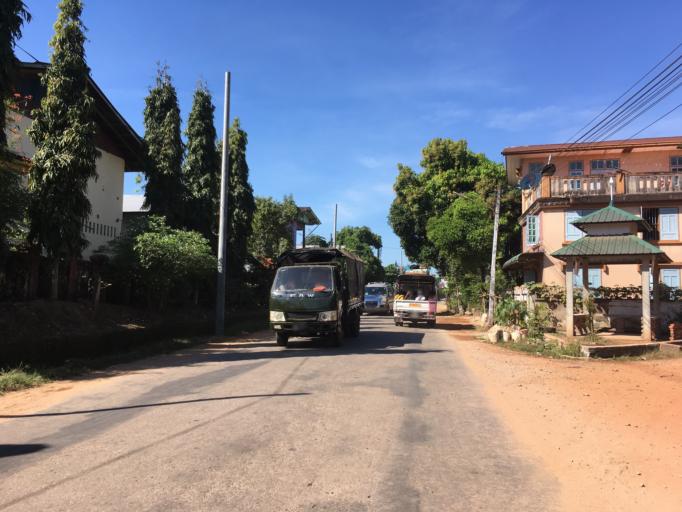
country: MM
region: Mon
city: Kyaikkami
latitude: 15.5093
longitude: 97.8523
